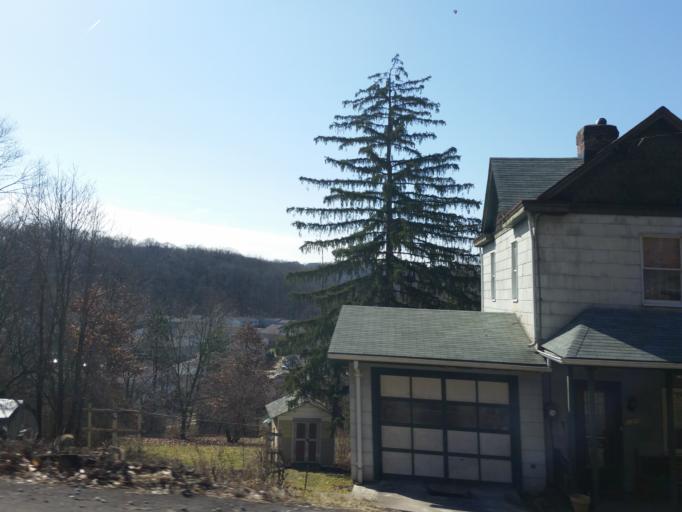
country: US
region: Pennsylvania
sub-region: Allegheny County
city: Ingram
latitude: 40.4512
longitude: -80.0746
